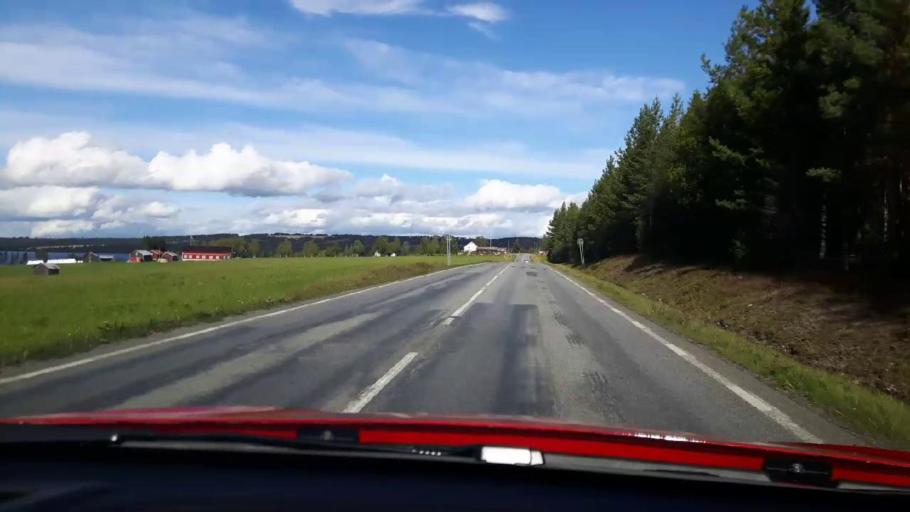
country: SE
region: Jaemtland
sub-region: OEstersunds Kommun
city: Ostersund
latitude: 63.1468
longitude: 14.4789
